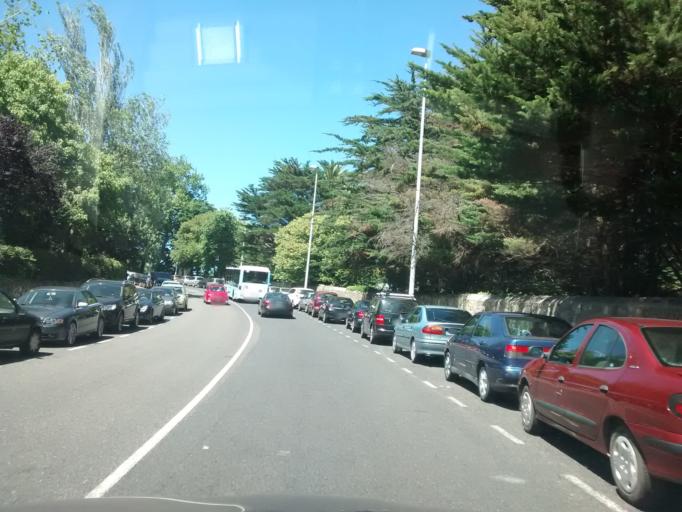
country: ES
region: Cantabria
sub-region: Provincia de Cantabria
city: Santander
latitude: 43.4824
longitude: -3.7877
